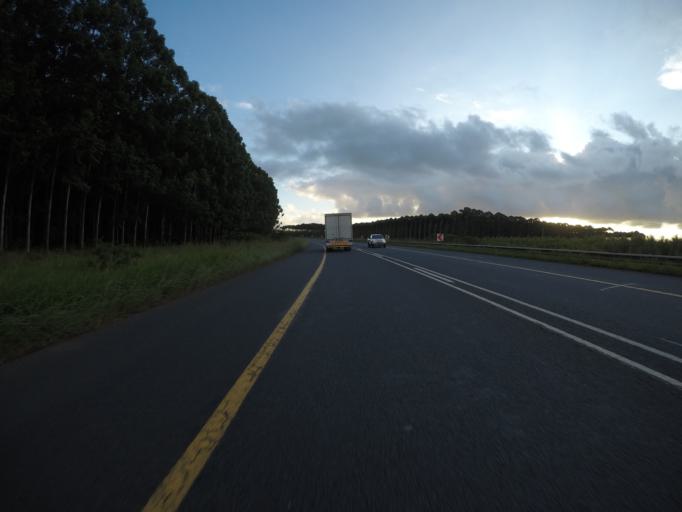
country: ZA
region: KwaZulu-Natal
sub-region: uThungulu District Municipality
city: KwaMbonambi
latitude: -28.5799
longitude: 32.1001
